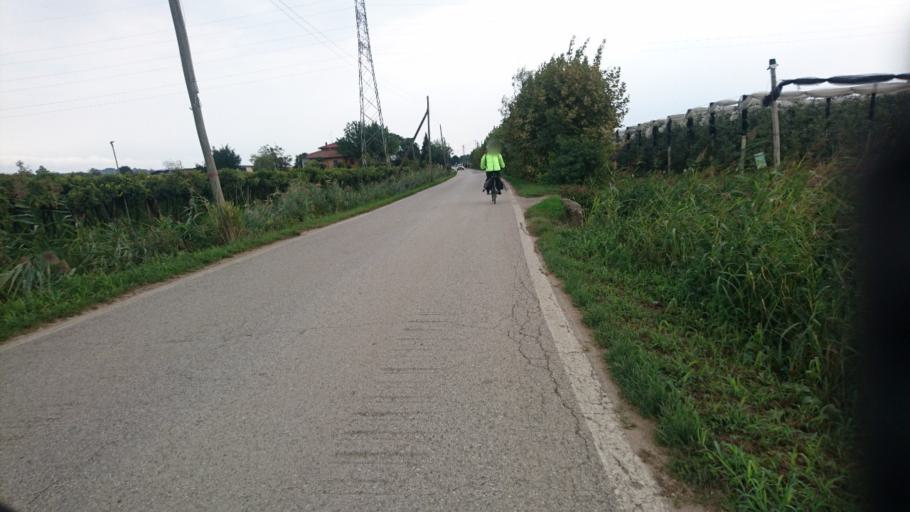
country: IT
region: Veneto
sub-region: Provincia di Verona
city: Caldierino-Rota
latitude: 45.4088
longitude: 11.1584
